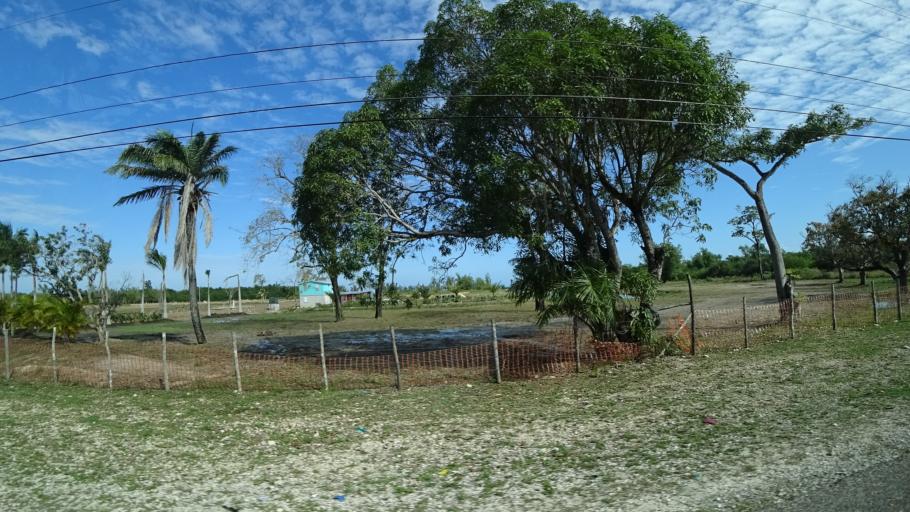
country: BZ
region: Belize
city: Belize City
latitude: 17.5448
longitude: -88.2700
